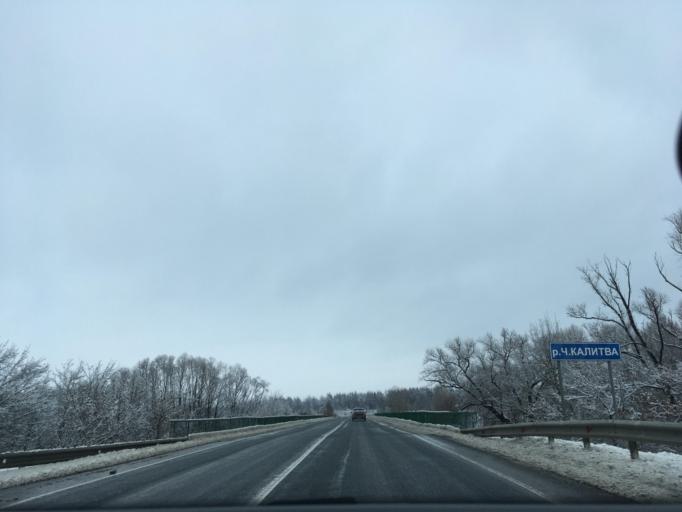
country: RU
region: Voronezj
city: Zabolotovka
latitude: 50.2456
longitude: 39.3784
